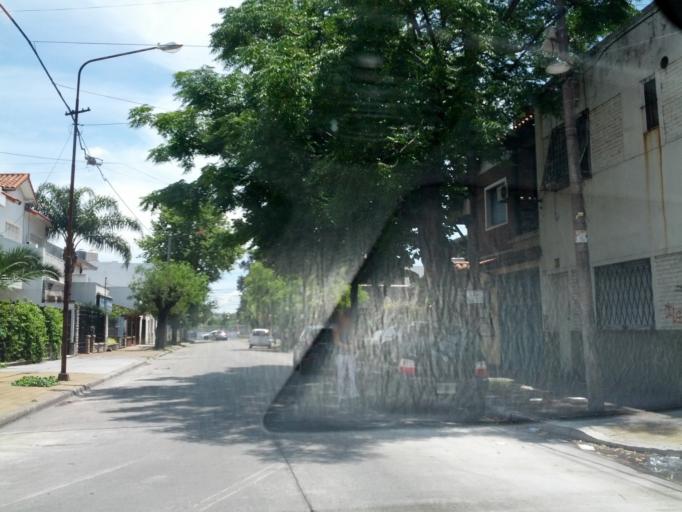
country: AR
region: Buenos Aires
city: San Justo
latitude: -34.6429
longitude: -58.5714
